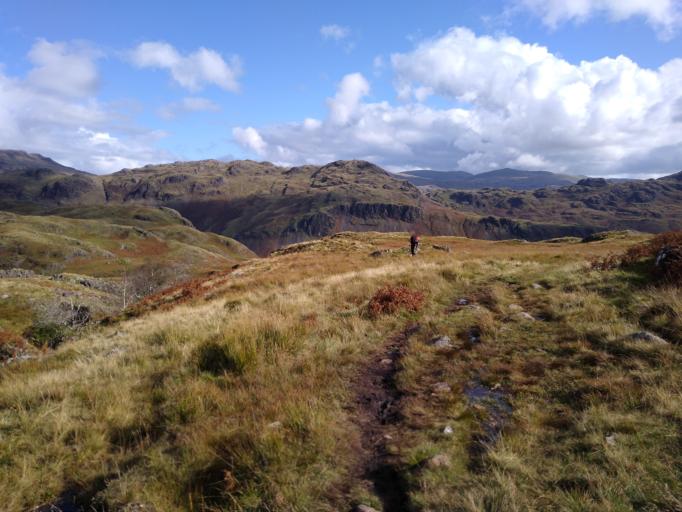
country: GB
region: England
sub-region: Cumbria
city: Keswick
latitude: 54.4153
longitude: -3.2234
